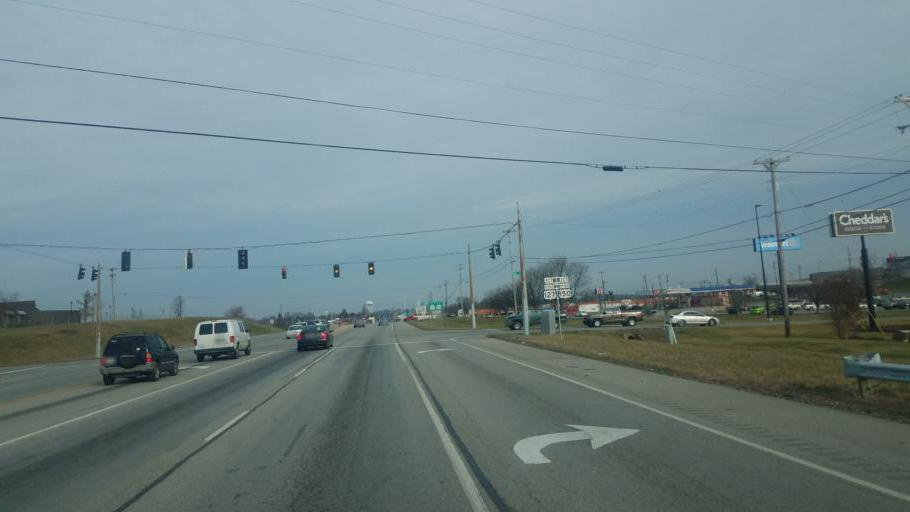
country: US
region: Kentucky
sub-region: Boyle County
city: Danville
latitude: 37.6142
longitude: -84.7744
